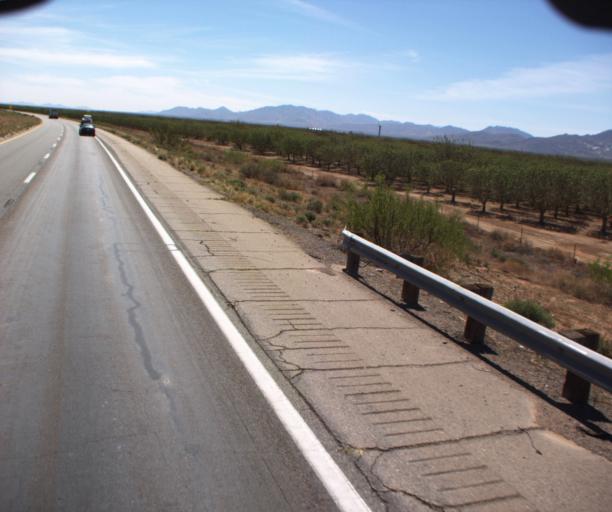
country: US
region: Arizona
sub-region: Cochise County
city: Willcox
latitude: 32.3215
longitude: -109.5006
